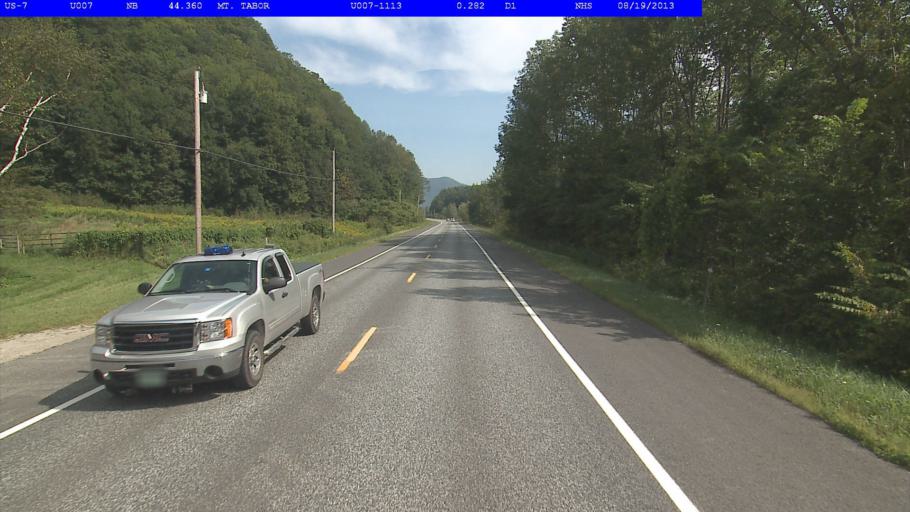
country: US
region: Vermont
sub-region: Bennington County
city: Manchester Center
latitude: 43.3091
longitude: -72.9940
